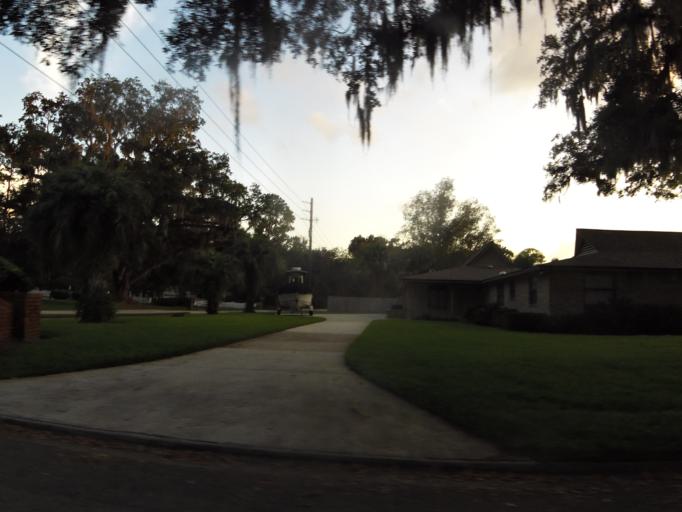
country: US
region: Florida
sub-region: Clay County
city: Orange Park
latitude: 30.1911
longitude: -81.6310
